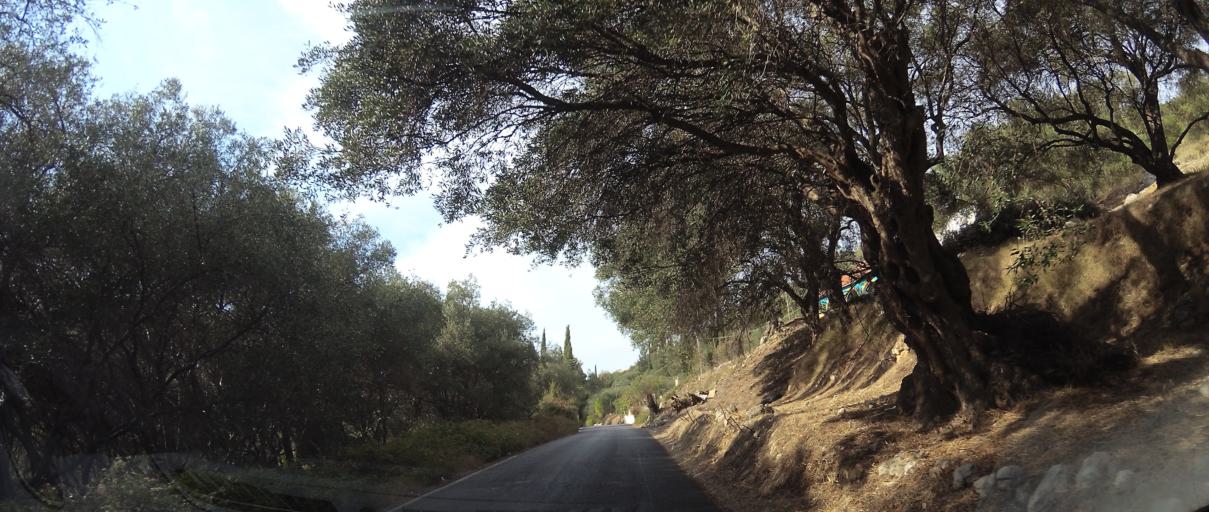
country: GR
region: Ionian Islands
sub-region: Nomos Kerkyras
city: Kynopiastes
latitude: 39.5477
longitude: 19.8673
